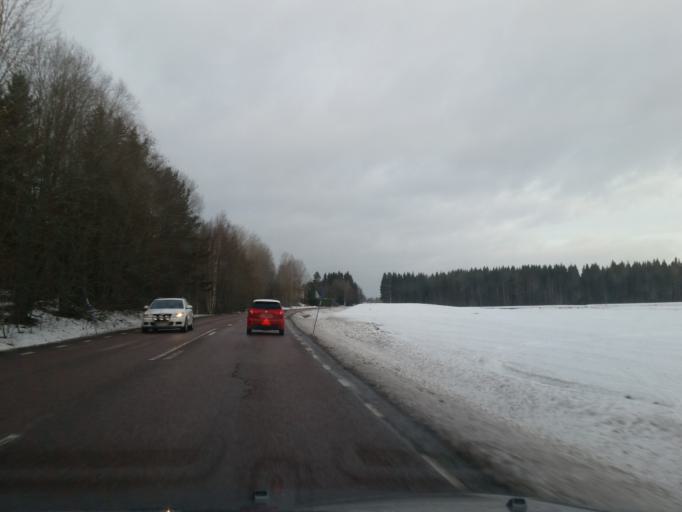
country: SE
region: Gaevleborg
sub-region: Sandvikens Kommun
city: Sandviken
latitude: 60.6647
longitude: 16.6933
